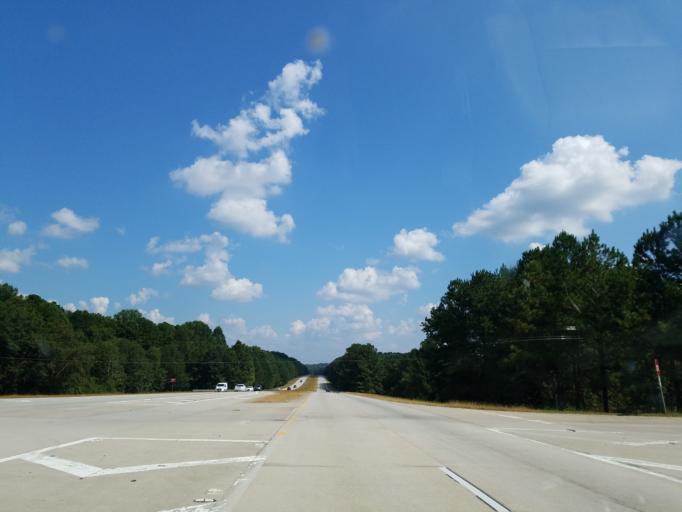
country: US
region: Georgia
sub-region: Barrow County
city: Russell
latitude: 33.9518
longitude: -83.6883
